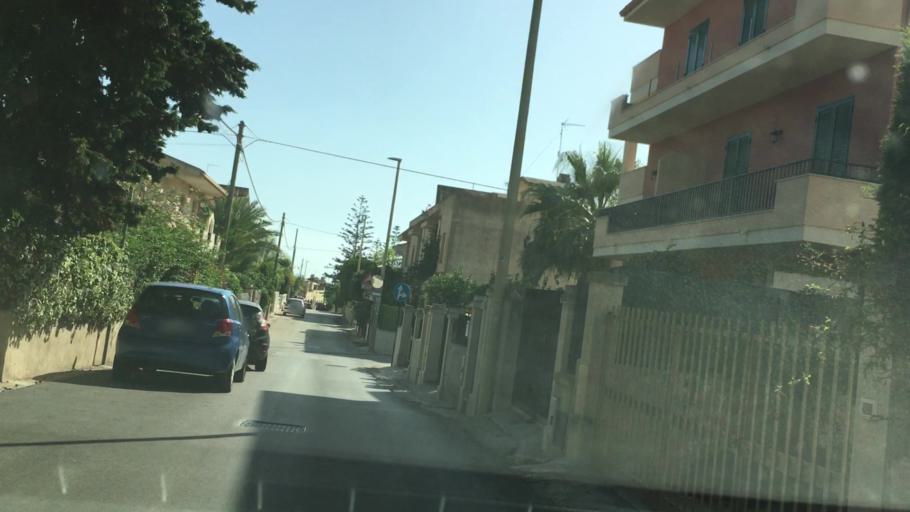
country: IT
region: Sicily
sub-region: Ragusa
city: Pozzallo
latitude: 36.7141
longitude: 14.7754
